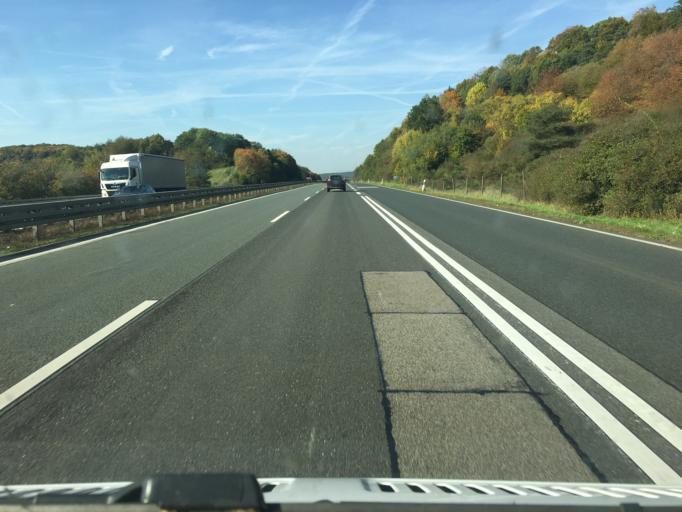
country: DE
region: Hesse
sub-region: Regierungsbezirk Giessen
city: Ehringshausen
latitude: 50.6133
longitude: 8.4121
